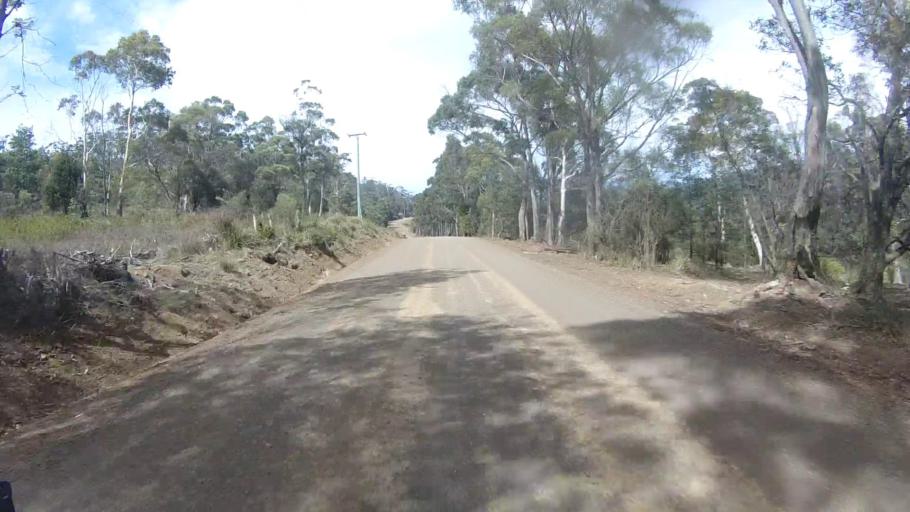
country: AU
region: Tasmania
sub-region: Sorell
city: Sorell
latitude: -42.6646
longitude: 147.8897
